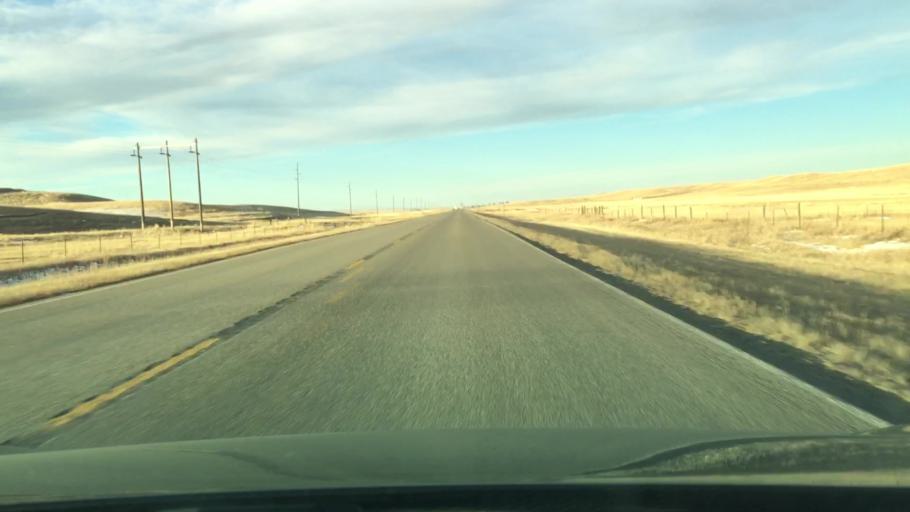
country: US
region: Montana
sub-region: Wheatland County
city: Harlowton
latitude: 46.7164
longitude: -109.7390
